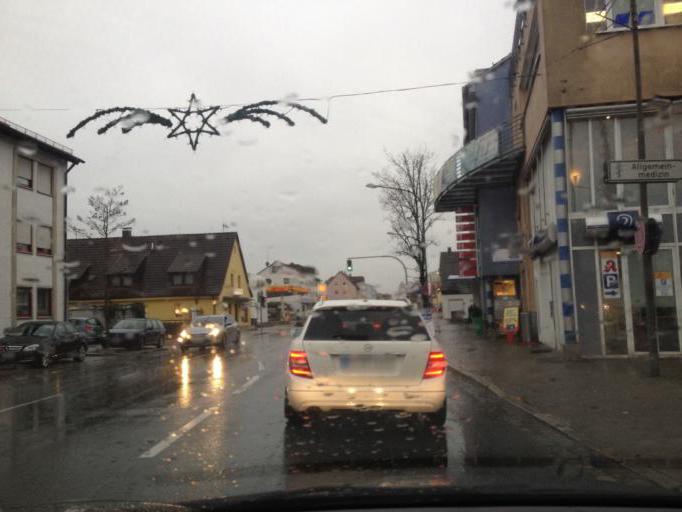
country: DE
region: Bavaria
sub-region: Regierungsbezirk Mittelfranken
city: Rothenbach an der Pegnitz
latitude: 49.4868
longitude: 11.2469
